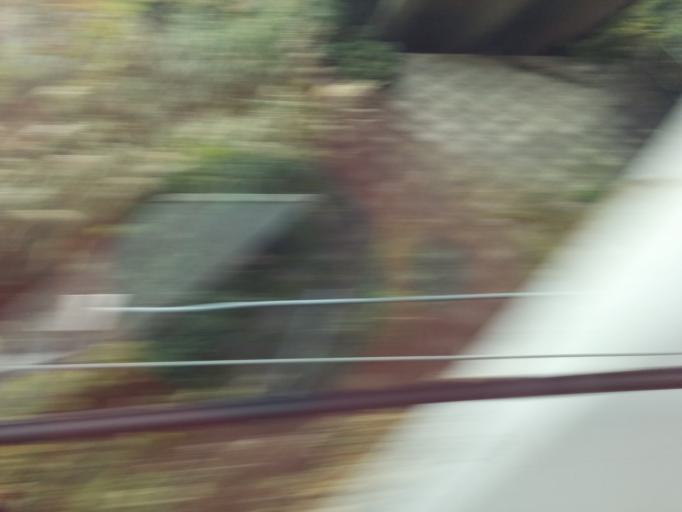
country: JP
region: Shizuoka
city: Numazu
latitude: 35.1451
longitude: 138.7990
